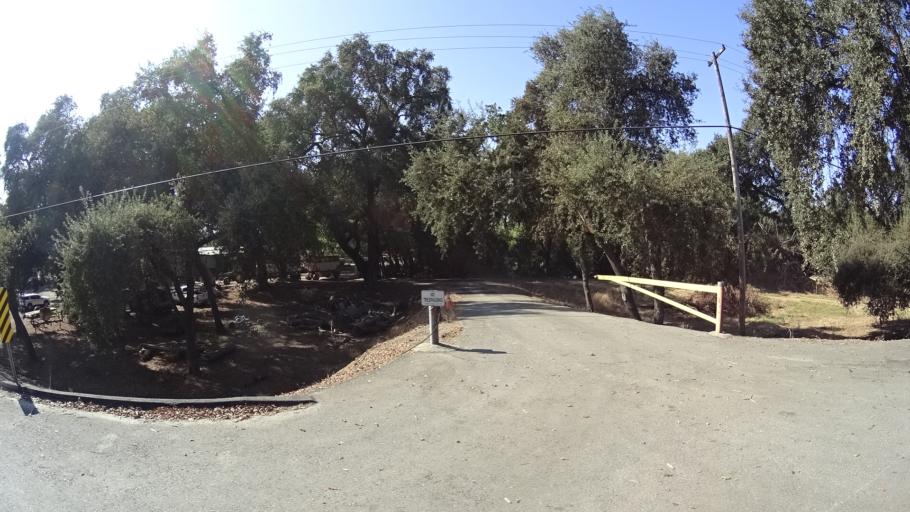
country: US
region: California
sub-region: Yolo County
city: West Sacramento
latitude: 38.6416
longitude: -121.5660
